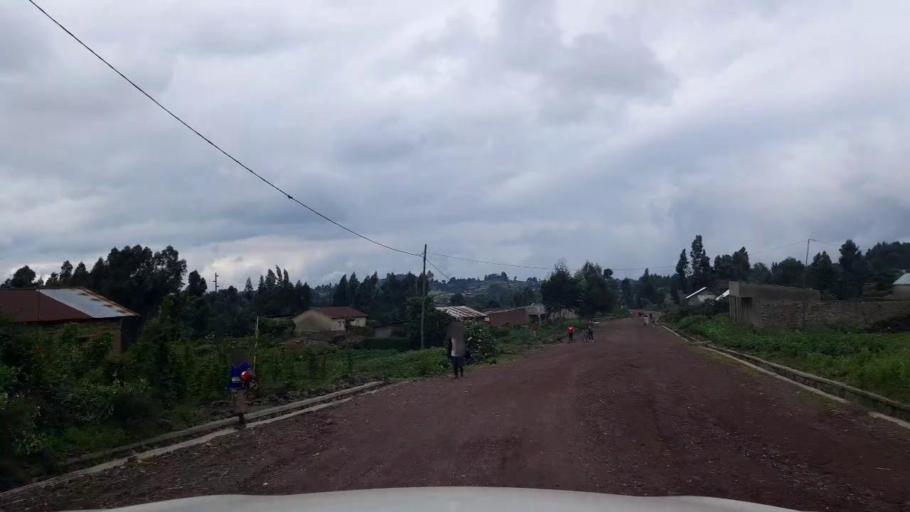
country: RW
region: Northern Province
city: Musanze
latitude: -1.5918
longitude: 29.4603
